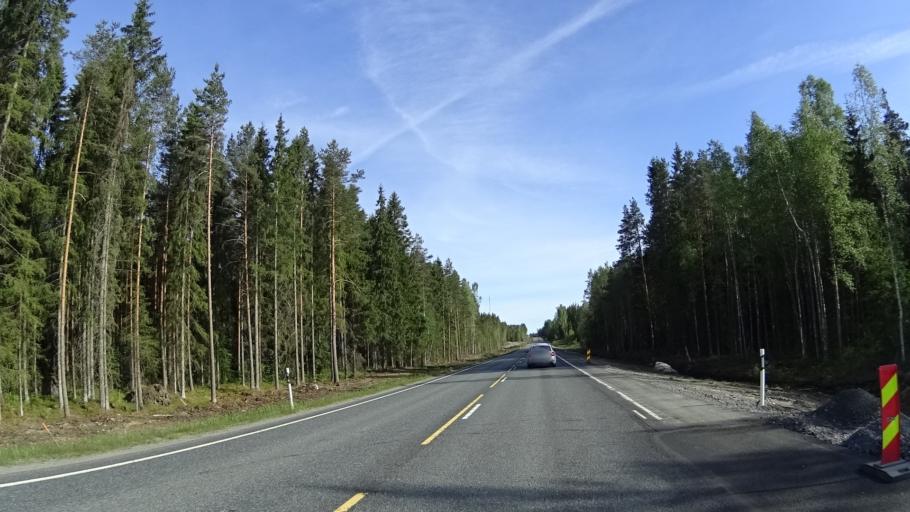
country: FI
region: Haeme
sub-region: Forssa
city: Tammela
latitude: 60.7323
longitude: 23.7472
